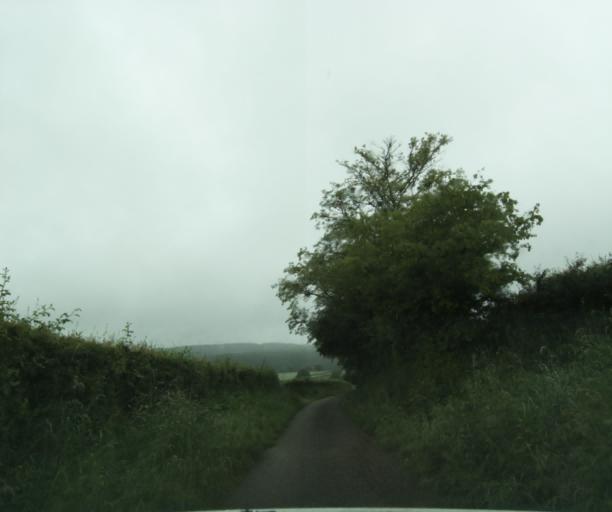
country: FR
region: Bourgogne
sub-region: Departement de Saone-et-Loire
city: Charolles
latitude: 46.4520
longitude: 4.3977
